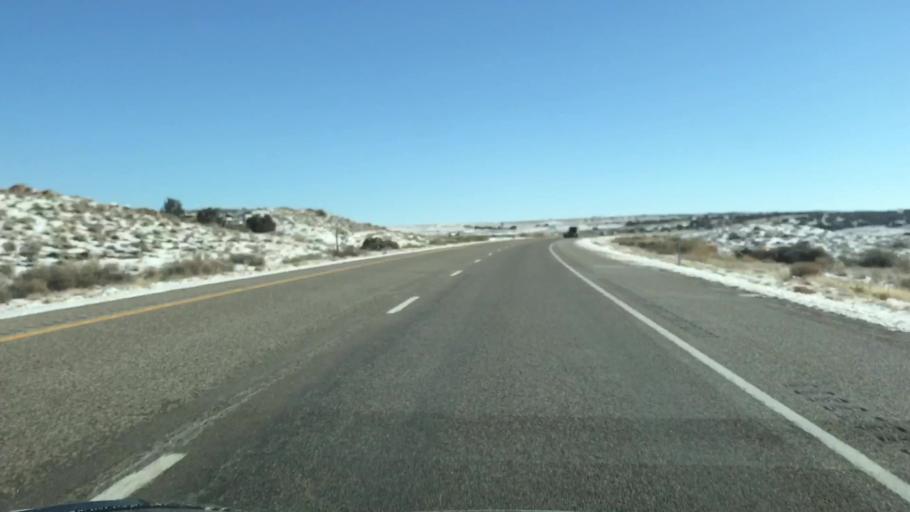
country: US
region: Colorado
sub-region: Mesa County
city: Loma
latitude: 39.1937
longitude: -109.0614
